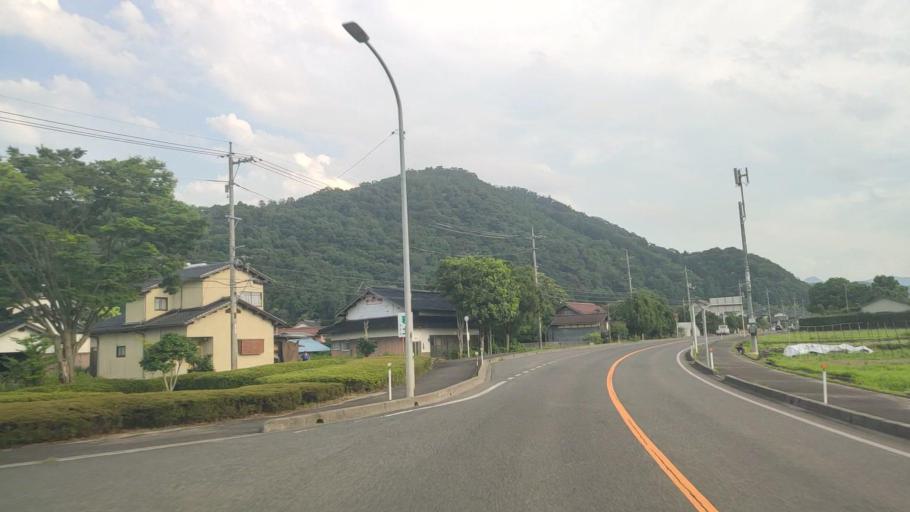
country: JP
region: Tottori
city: Kurayoshi
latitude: 35.3876
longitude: 133.7807
